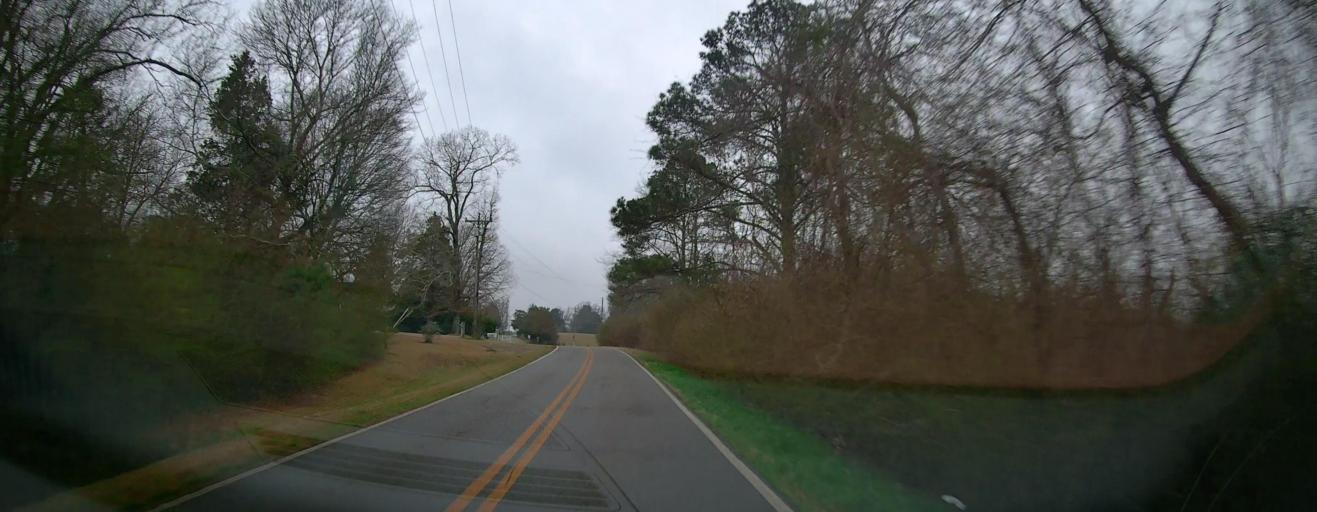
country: US
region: Georgia
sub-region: Lamar County
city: Barnesville
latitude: 33.0905
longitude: -84.0727
